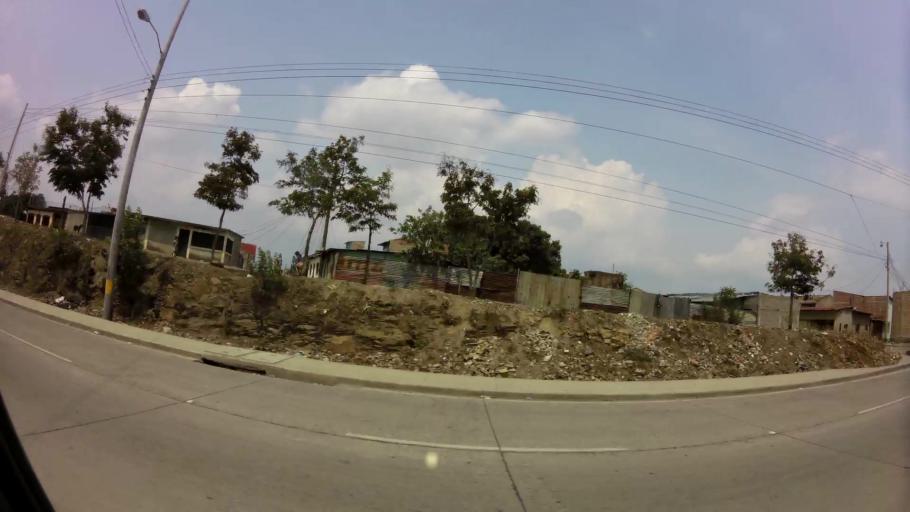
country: HN
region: Francisco Morazan
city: Tegucigalpa
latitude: 14.0793
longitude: -87.2368
